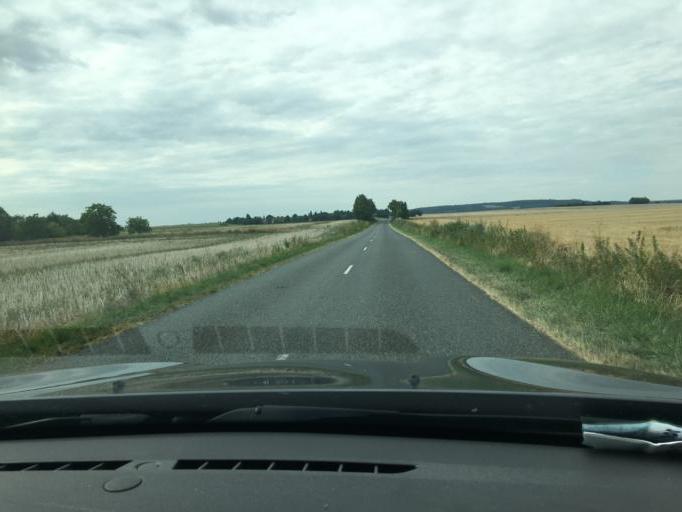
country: FR
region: Centre
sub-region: Departement du Cher
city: Rians
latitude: 47.2075
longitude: 2.5690
